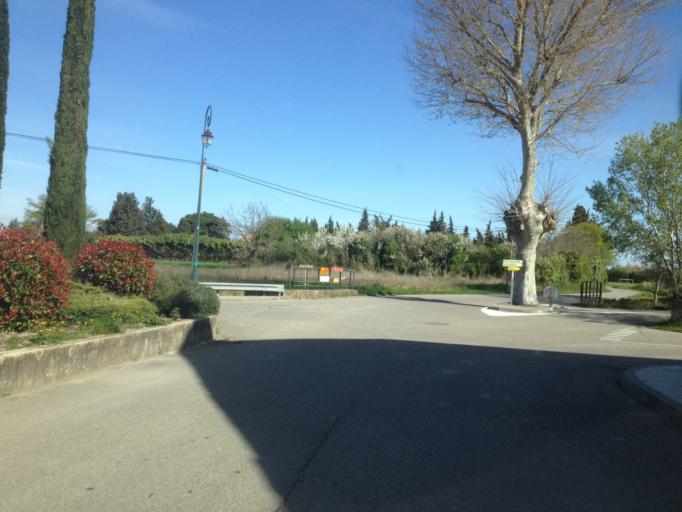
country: FR
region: Provence-Alpes-Cote d'Azur
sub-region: Departement du Vaucluse
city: Caderousse
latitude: 44.1073
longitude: 4.7549
